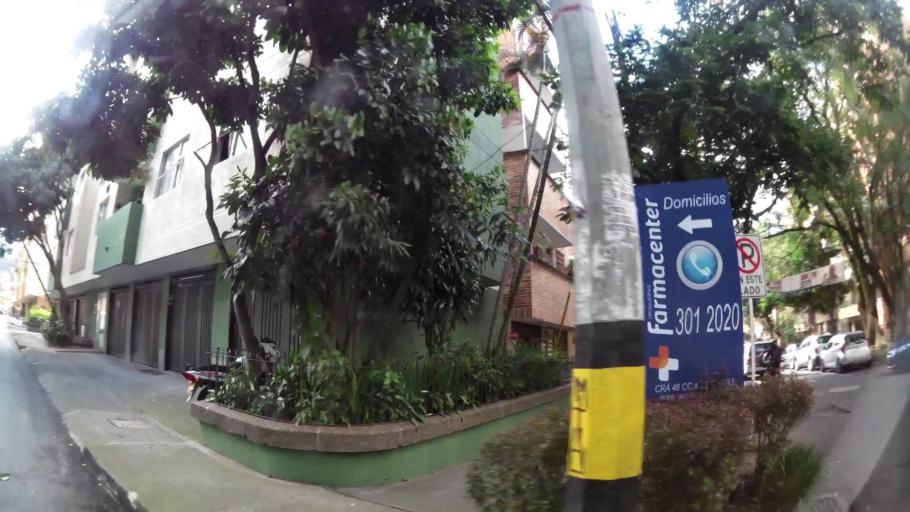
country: CO
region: Antioquia
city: Sabaneta
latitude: 6.1526
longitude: -75.6184
